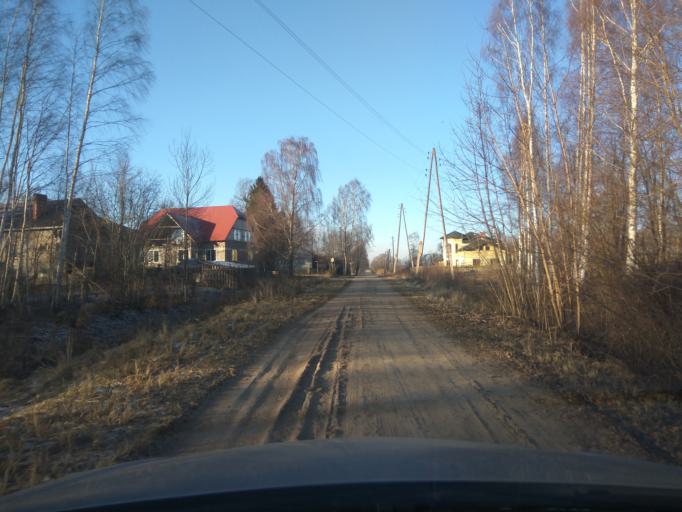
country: LV
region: Kuldigas Rajons
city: Kuldiga
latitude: 56.9663
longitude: 21.9494
